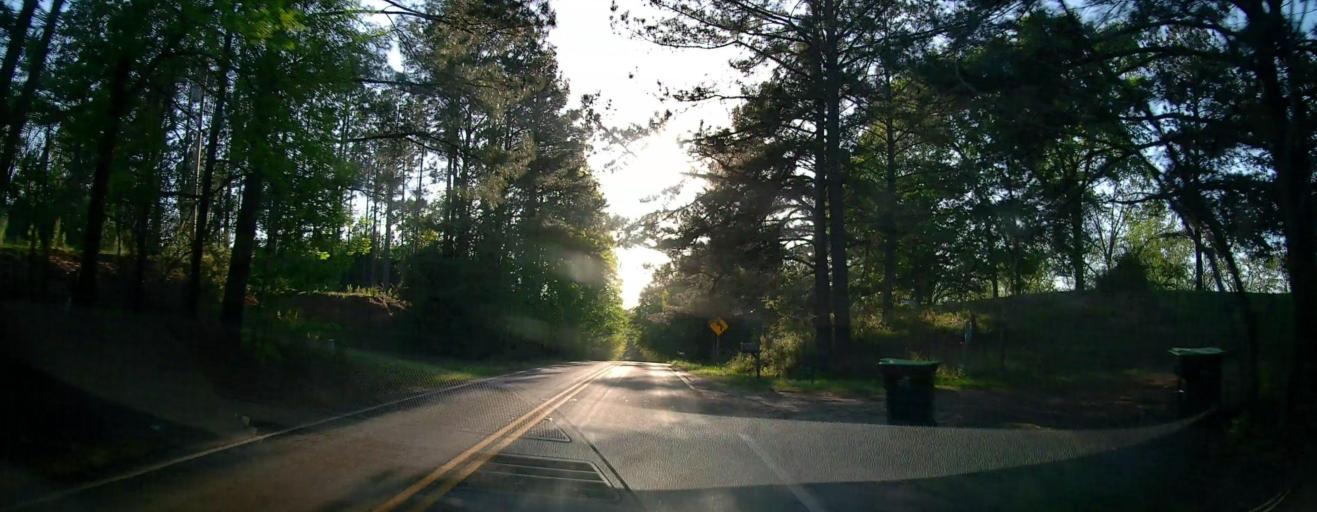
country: US
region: Georgia
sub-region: Schley County
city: Ellaville
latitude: 32.3221
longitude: -84.2356
